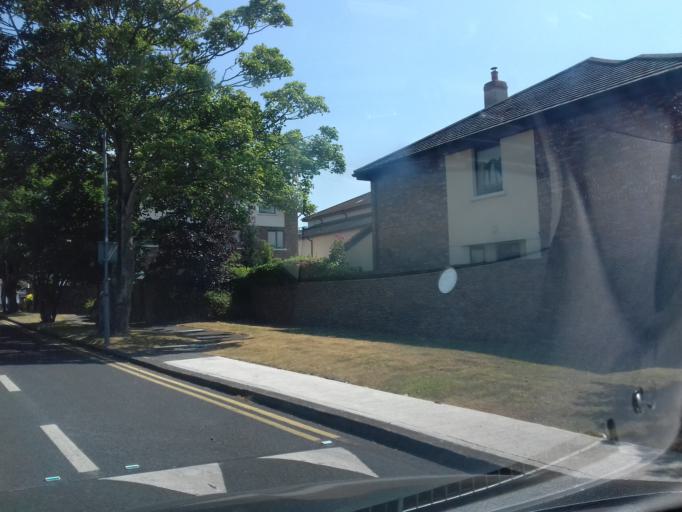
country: IE
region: Leinster
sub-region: Fingal County
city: Baldoyle
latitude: 53.3905
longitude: -6.1253
